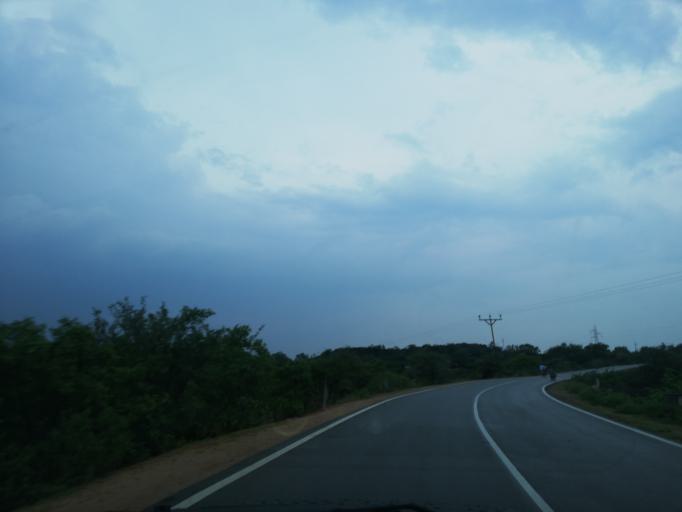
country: IN
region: Andhra Pradesh
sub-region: Guntur
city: Macherla
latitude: 16.6602
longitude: 79.2847
